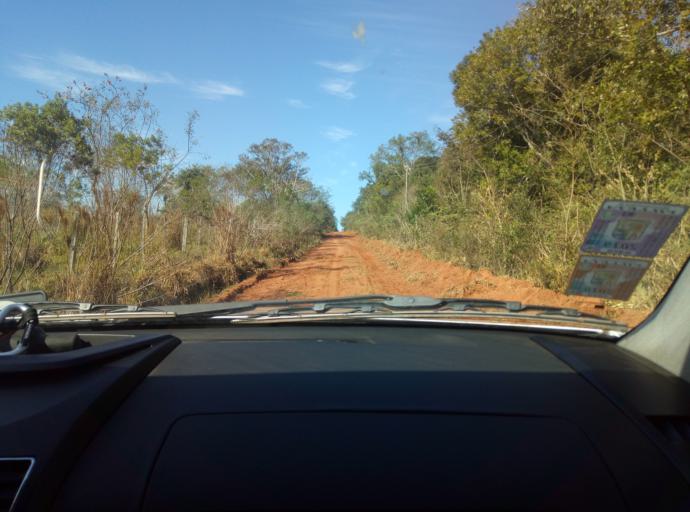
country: PY
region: Caaguazu
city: Carayao
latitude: -25.1700
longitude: -56.3005
